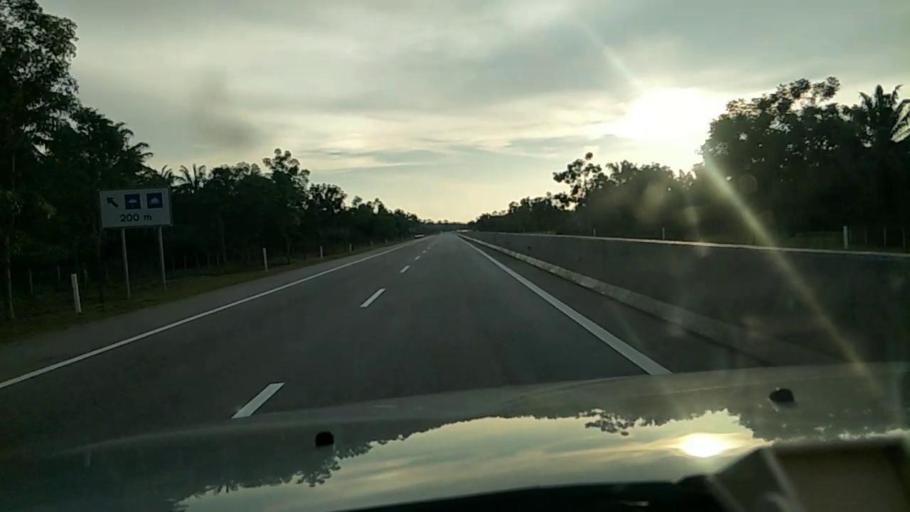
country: MY
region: Selangor
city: Batu Arang
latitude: 3.2882
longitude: 101.4260
